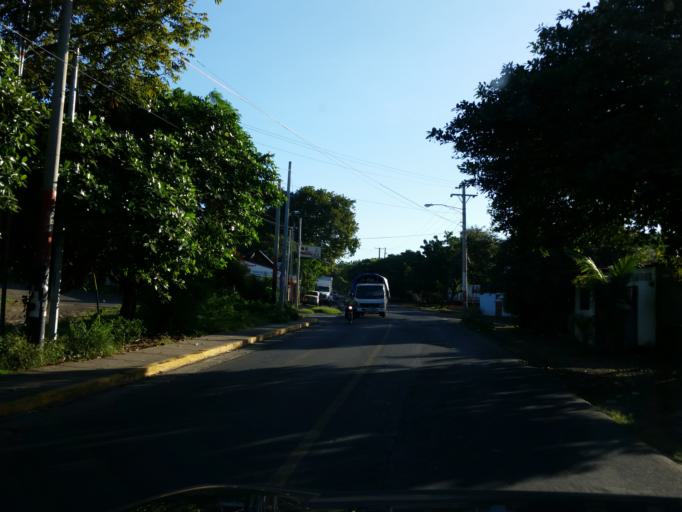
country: NI
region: Managua
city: Managua
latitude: 12.1381
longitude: -86.2986
